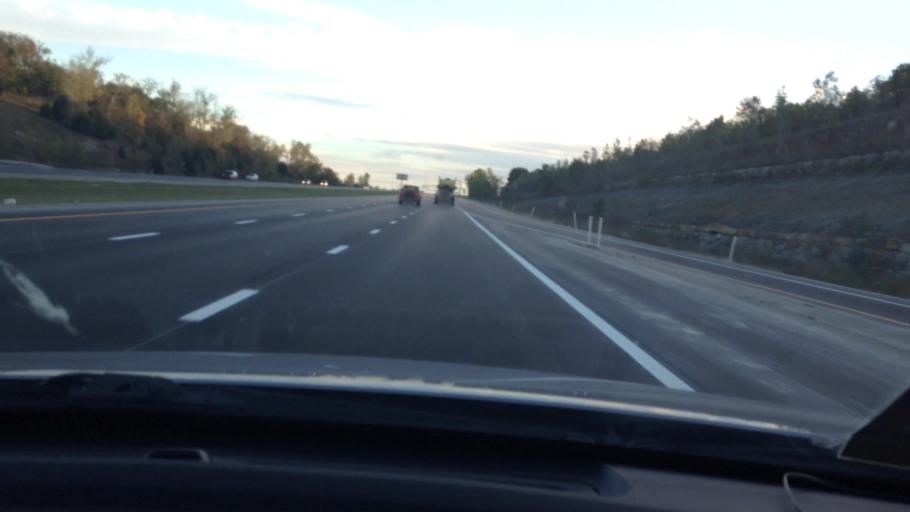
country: US
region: Kansas
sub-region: Wyandotte County
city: Edwardsville
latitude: 39.1552
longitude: -94.8212
